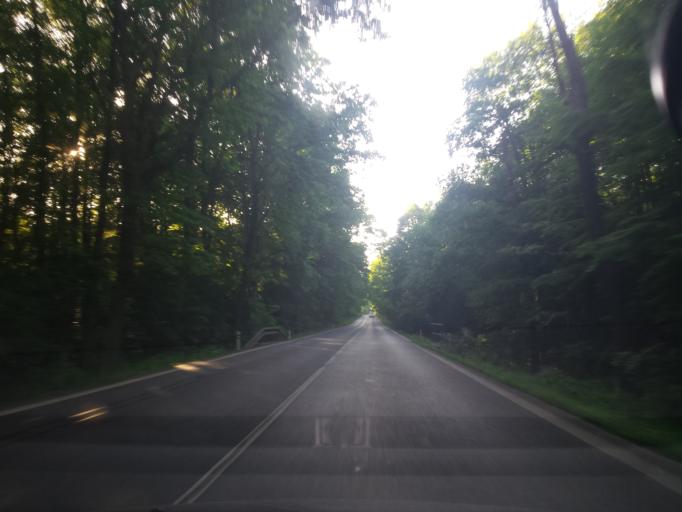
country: CZ
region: Liberecky
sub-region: Okres Ceska Lipa
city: Ceska Lipa
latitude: 50.6197
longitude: 14.5408
